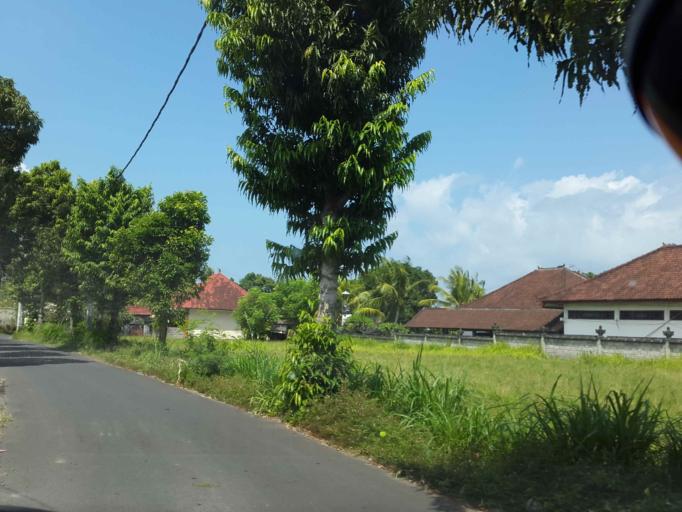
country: ID
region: Bali
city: Klungkung
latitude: -8.5545
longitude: 115.3788
